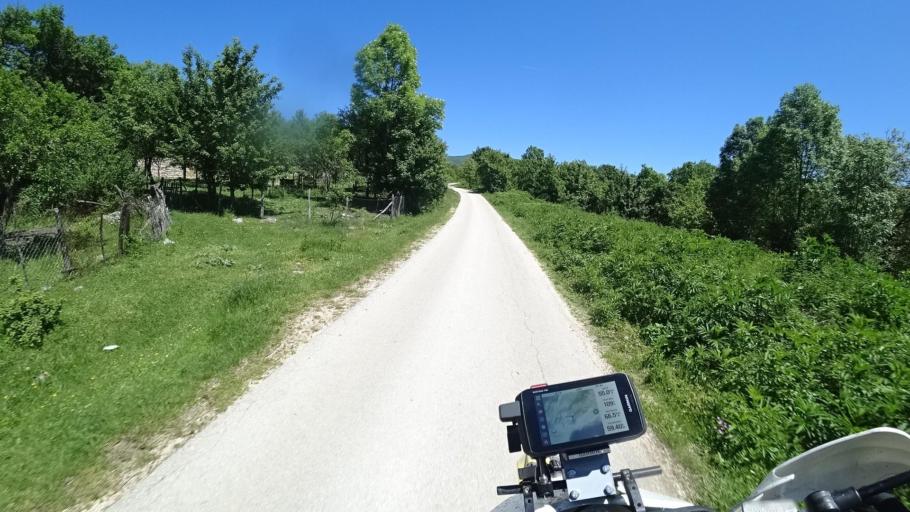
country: BA
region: Republika Srpska
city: Mrkonjic Grad
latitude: 44.4730
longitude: 17.1987
